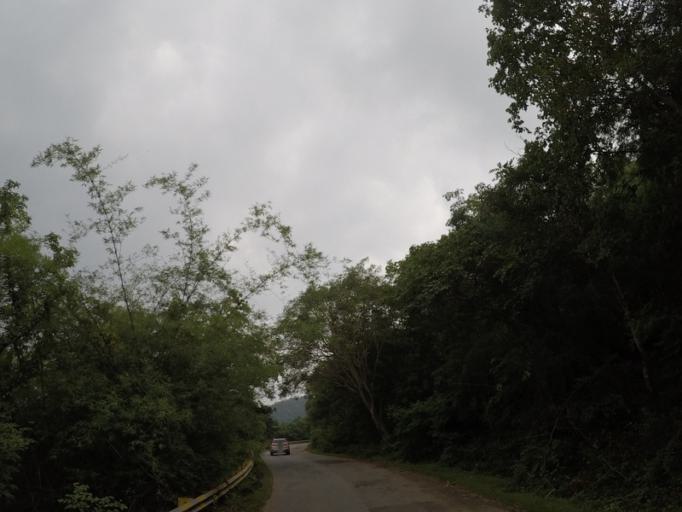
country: IN
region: Karnataka
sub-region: Chikmagalur
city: Birur
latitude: 13.5325
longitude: 75.8203
